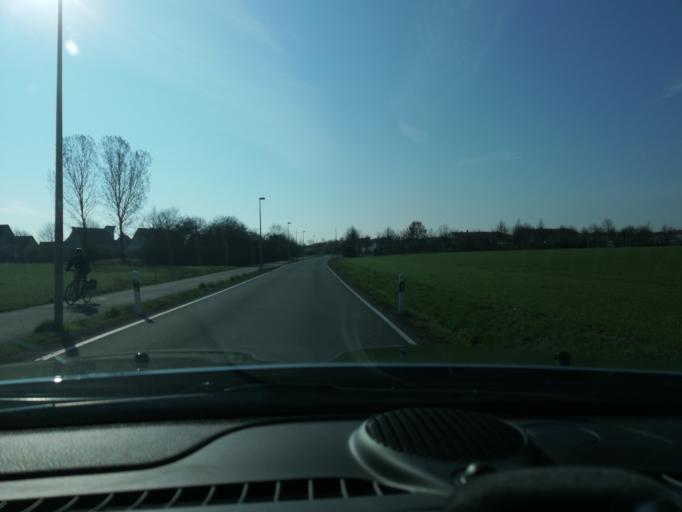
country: DE
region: Bavaria
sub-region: Regierungsbezirk Mittelfranken
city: Hessdorf
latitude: 49.5993
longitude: 10.9439
